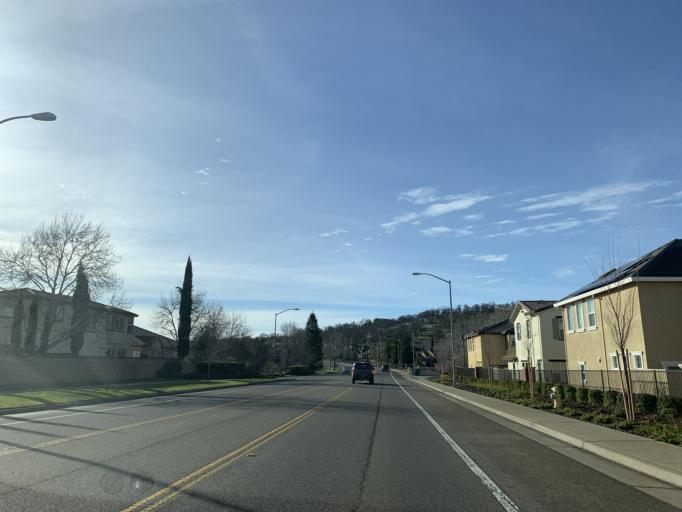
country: US
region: California
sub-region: El Dorado County
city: El Dorado Hills
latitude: 38.6760
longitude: -121.1103
